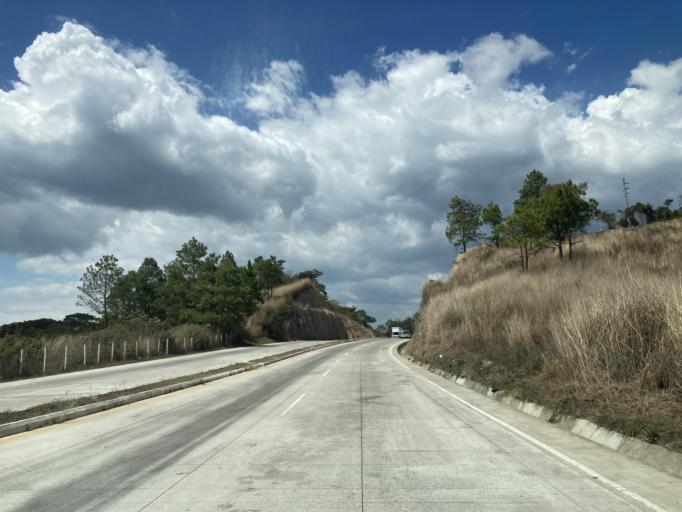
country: GT
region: Santa Rosa
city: Barberena
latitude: 14.2956
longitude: -90.3586
